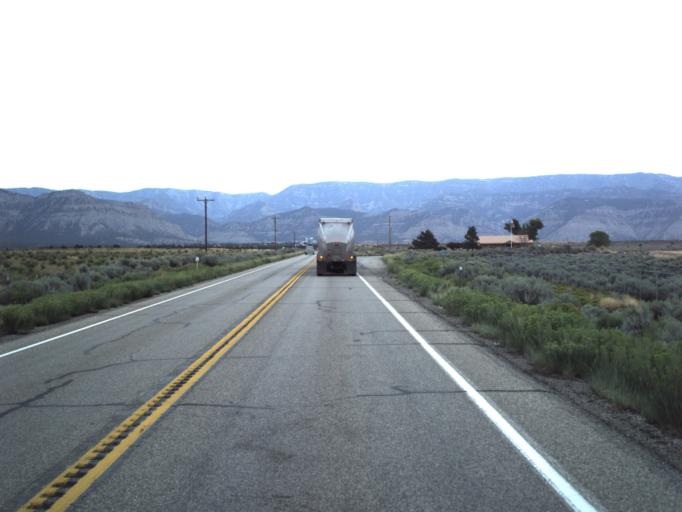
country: US
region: Utah
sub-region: Carbon County
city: East Carbon City
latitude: 39.5358
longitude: -110.4648
